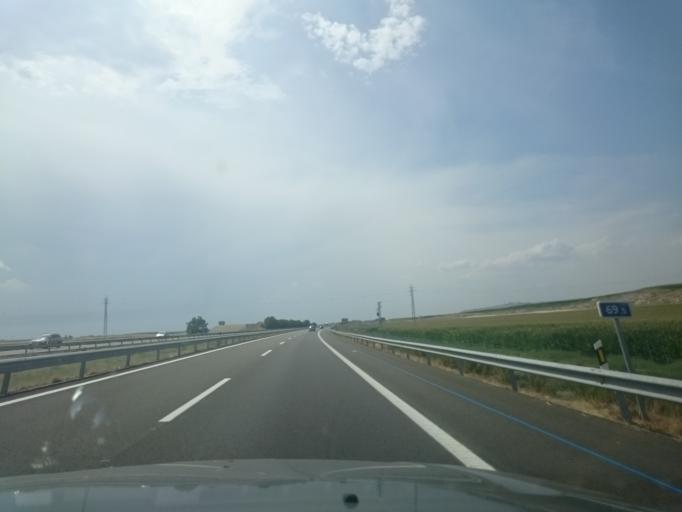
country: ES
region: Aragon
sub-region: Provincia de Zaragoza
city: Bujaraloz
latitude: 41.5175
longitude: -0.1466
